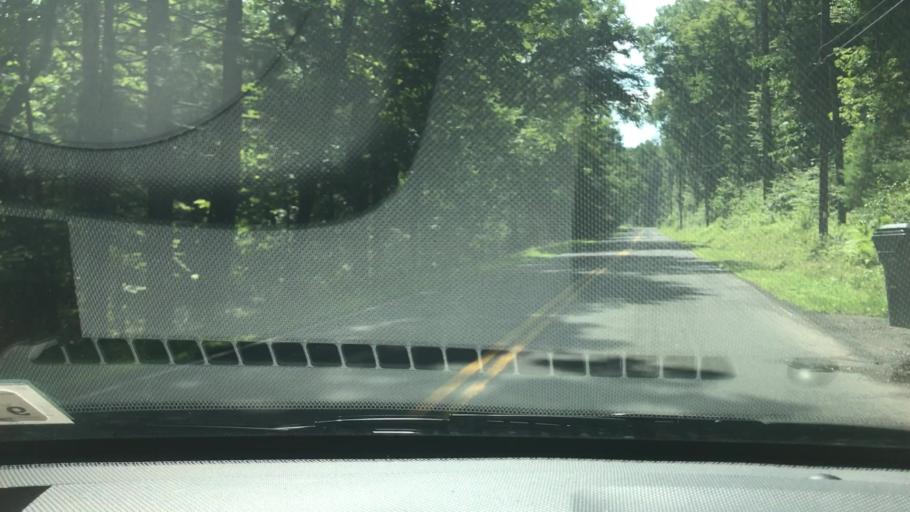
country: US
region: New York
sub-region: Ulster County
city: Shokan
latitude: 41.9598
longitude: -74.2694
